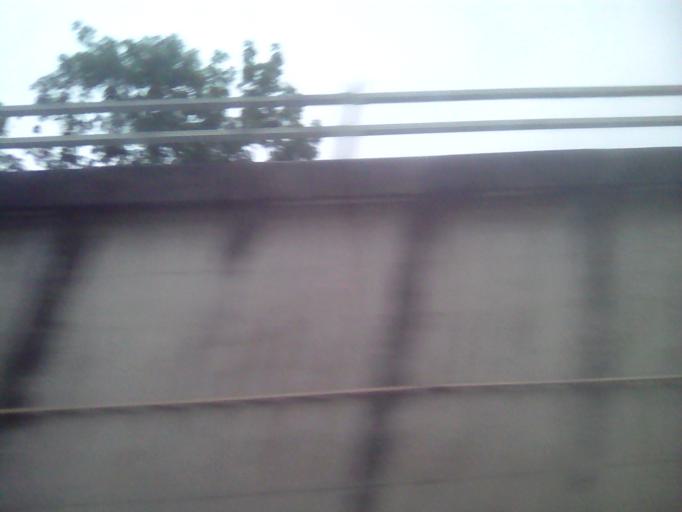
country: MY
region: Penang
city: Perai
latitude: 5.3994
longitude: 100.4076
